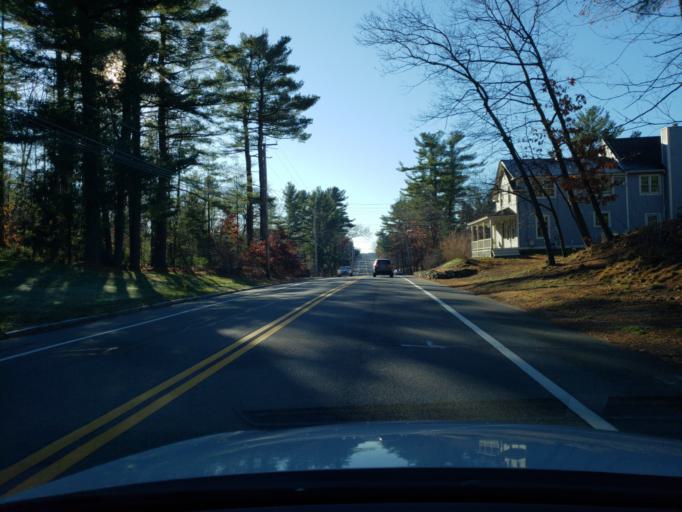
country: US
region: Massachusetts
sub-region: Essex County
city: Andover
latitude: 42.6120
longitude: -71.1236
